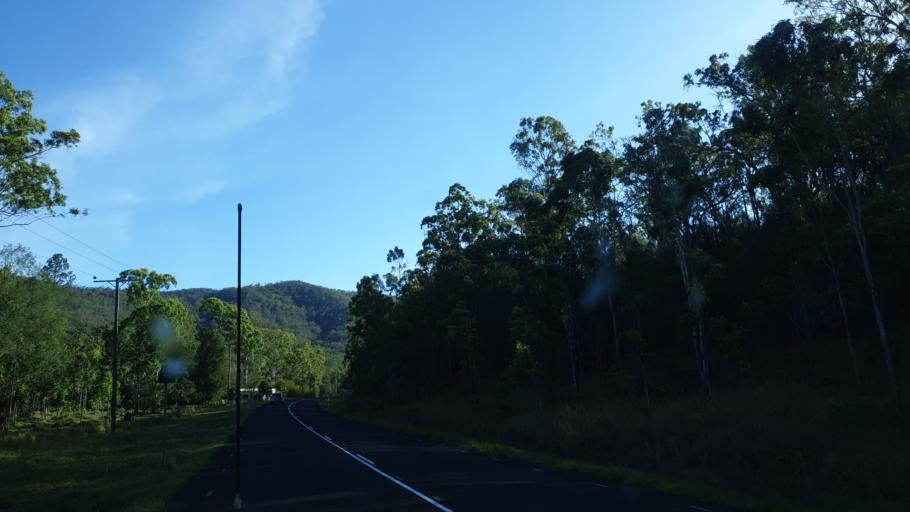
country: AU
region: Queensland
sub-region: Tablelands
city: Atherton
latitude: -17.3258
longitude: 145.4390
